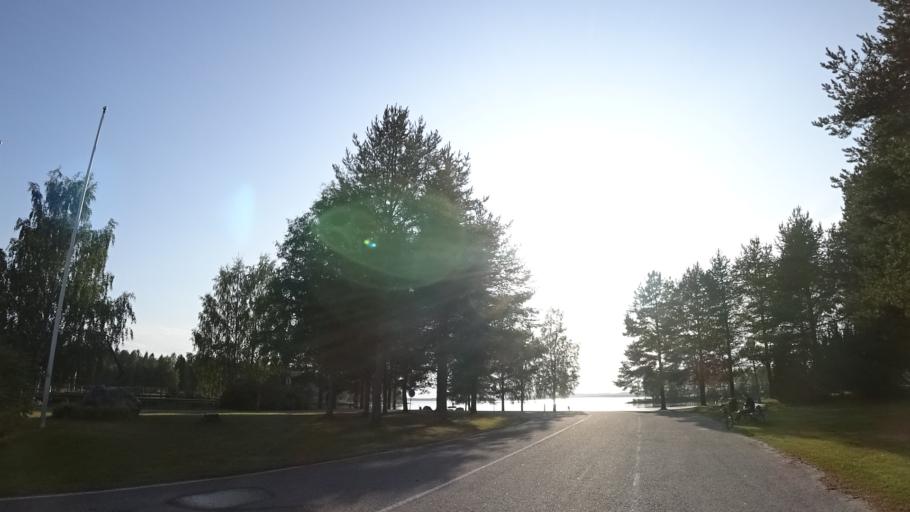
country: FI
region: North Karelia
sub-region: Pielisen Karjala
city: Lieksa
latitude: 63.3088
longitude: 30.0126
